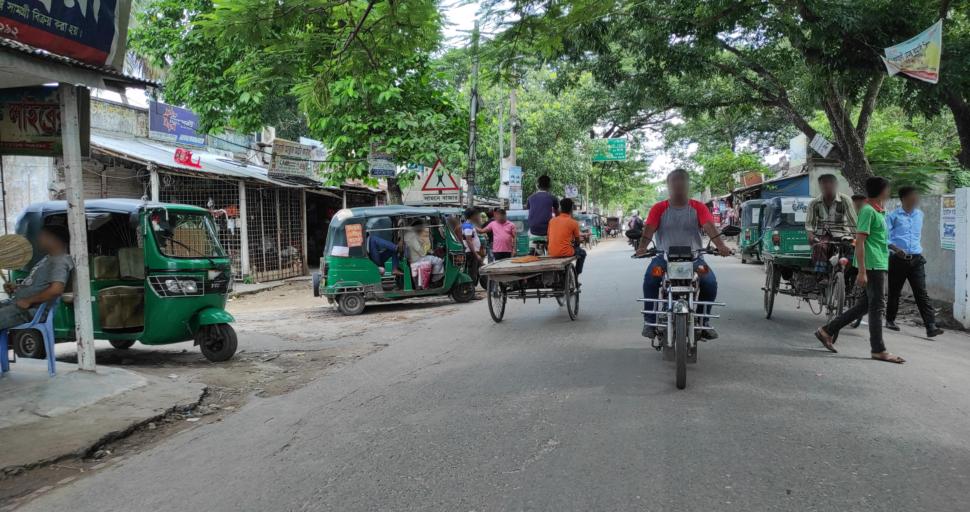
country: BD
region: Rajshahi
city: Rajshahi
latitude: 24.3715
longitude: 88.8391
